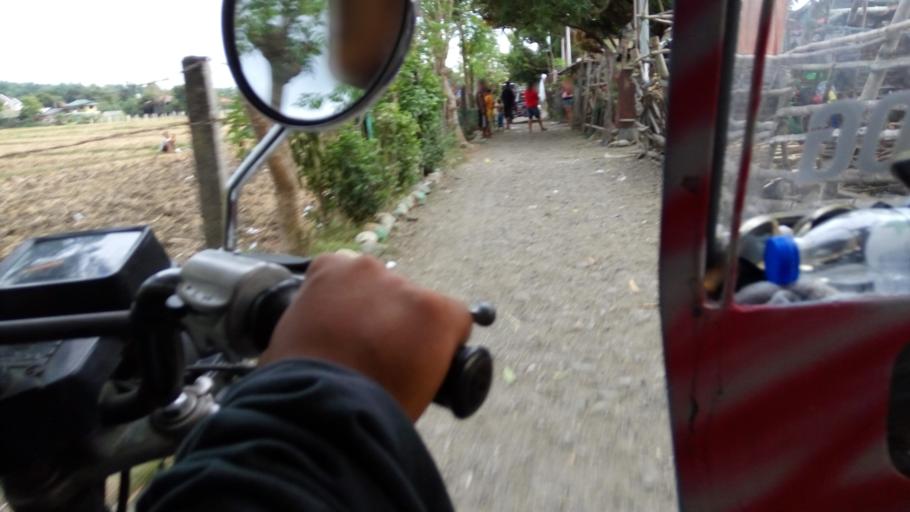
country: PH
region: Ilocos
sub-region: Province of La Union
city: Damortis
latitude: 16.2541
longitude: 120.4004
